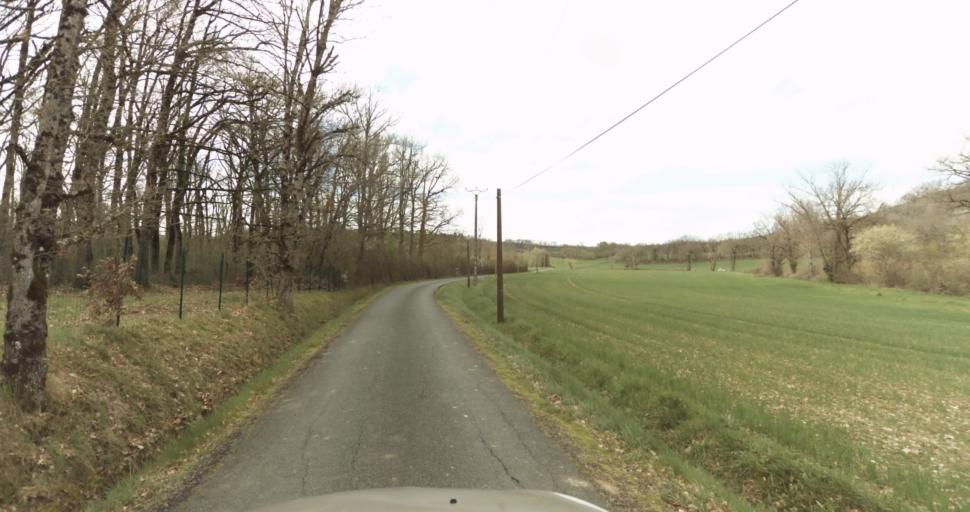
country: FR
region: Midi-Pyrenees
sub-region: Departement du Tarn
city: Frejairolles
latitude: 43.8795
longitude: 2.1982
